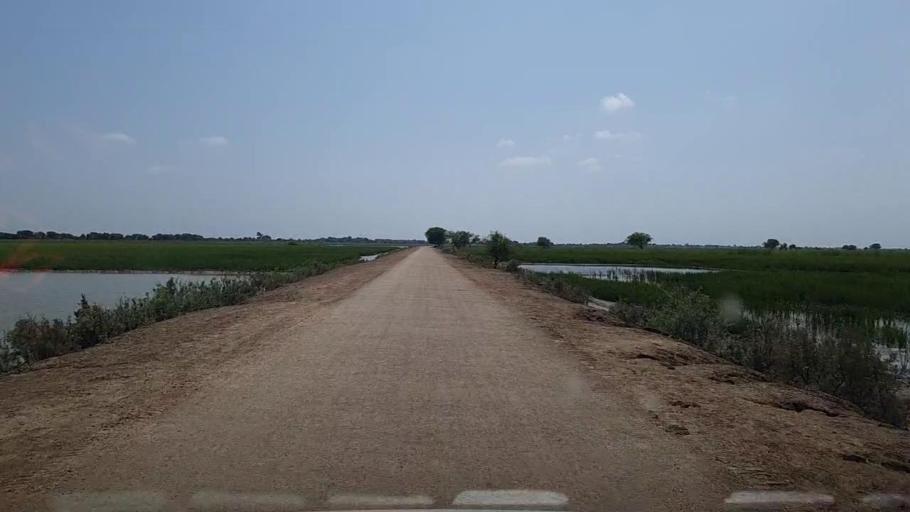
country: PK
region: Sindh
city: Kario
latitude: 24.8380
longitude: 68.7029
